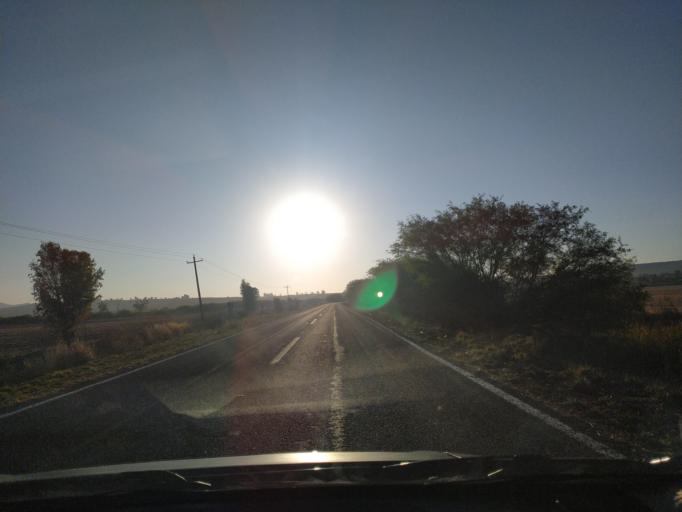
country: MX
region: Guanajuato
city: Ciudad Manuel Doblado
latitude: 20.7358
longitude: -101.8399
